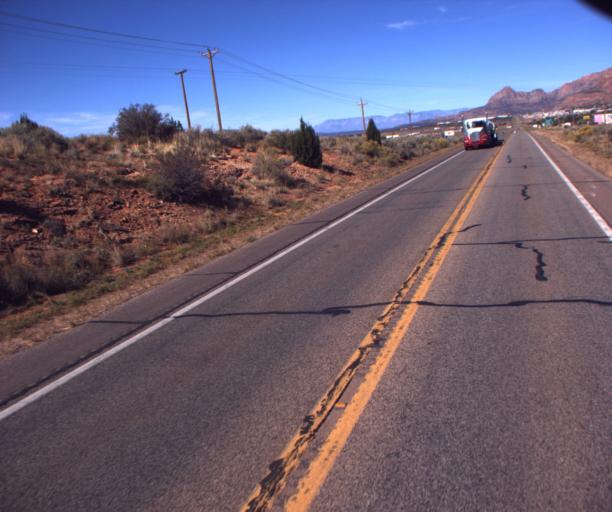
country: US
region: Arizona
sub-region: Mohave County
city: Colorado City
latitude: 36.9685
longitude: -112.9734
